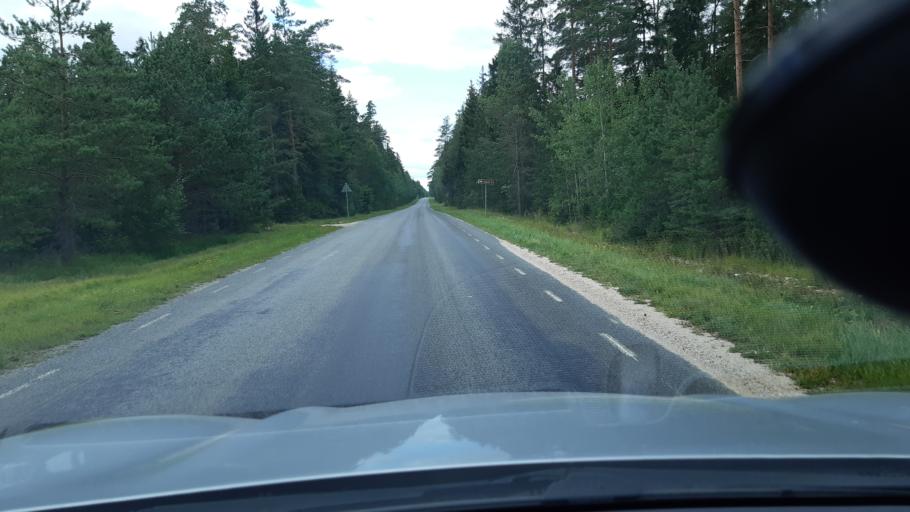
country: EE
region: Raplamaa
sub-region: Rapla vald
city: Rapla
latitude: 58.8982
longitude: 24.6965
